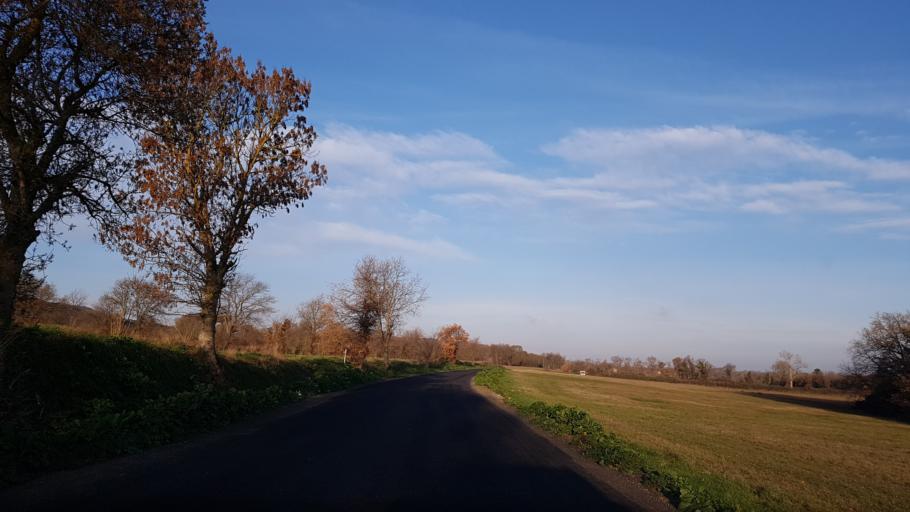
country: FR
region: Languedoc-Roussillon
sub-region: Departement de l'Aude
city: Villeneuve-la-Comptal
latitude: 43.2803
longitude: 1.9392
